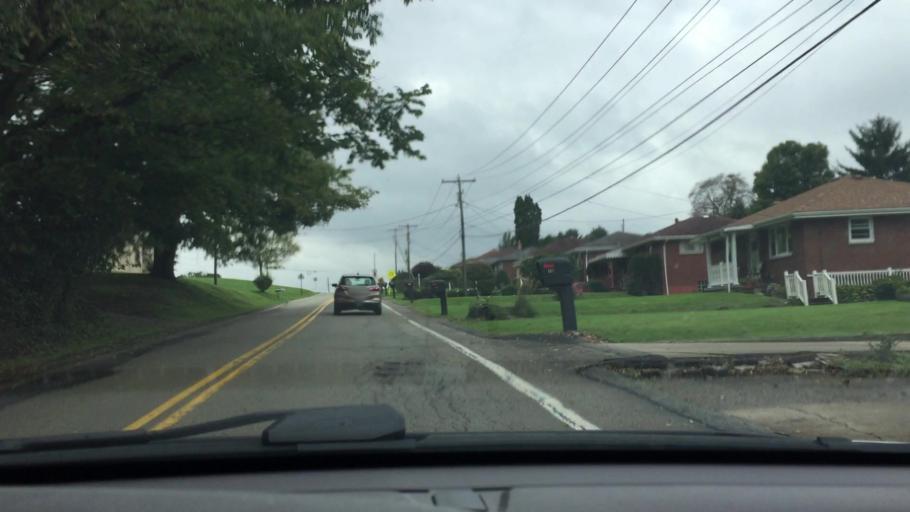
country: US
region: Pennsylvania
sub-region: Westmoreland County
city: North Belle Vernon
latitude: 40.1417
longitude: -79.8720
